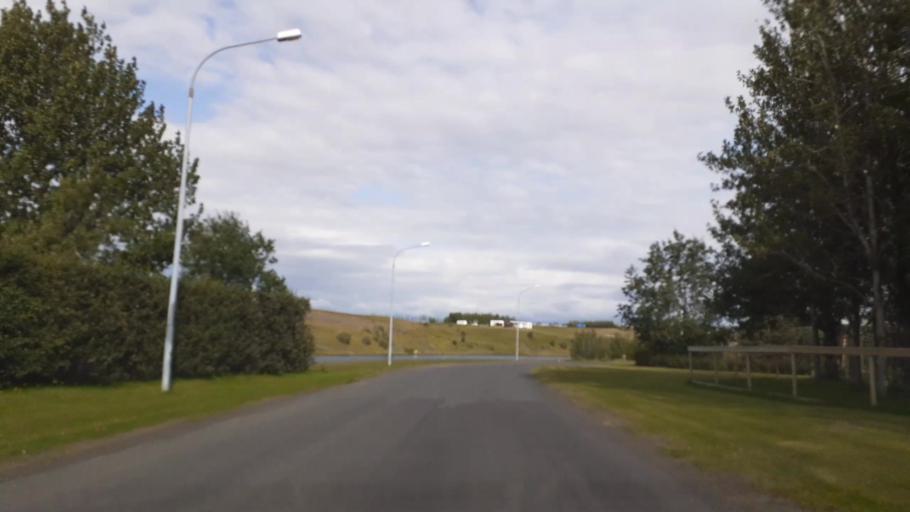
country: IS
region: South
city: Vestmannaeyjar
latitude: 63.8406
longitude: -20.4005
